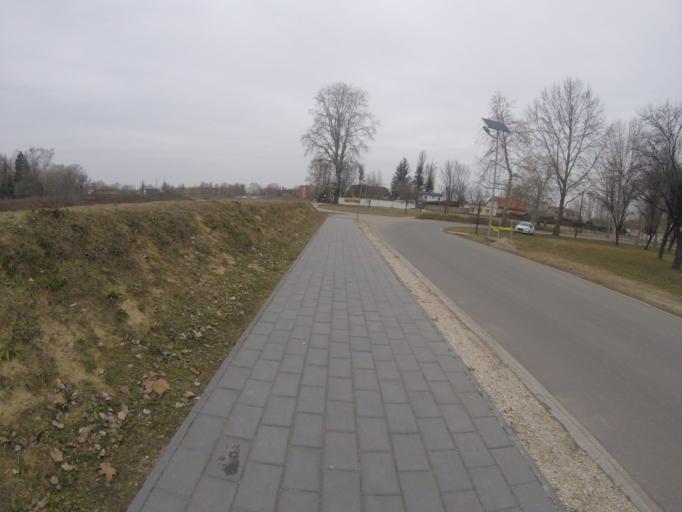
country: HU
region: Bacs-Kiskun
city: Baja
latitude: 46.1769
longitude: 18.9405
